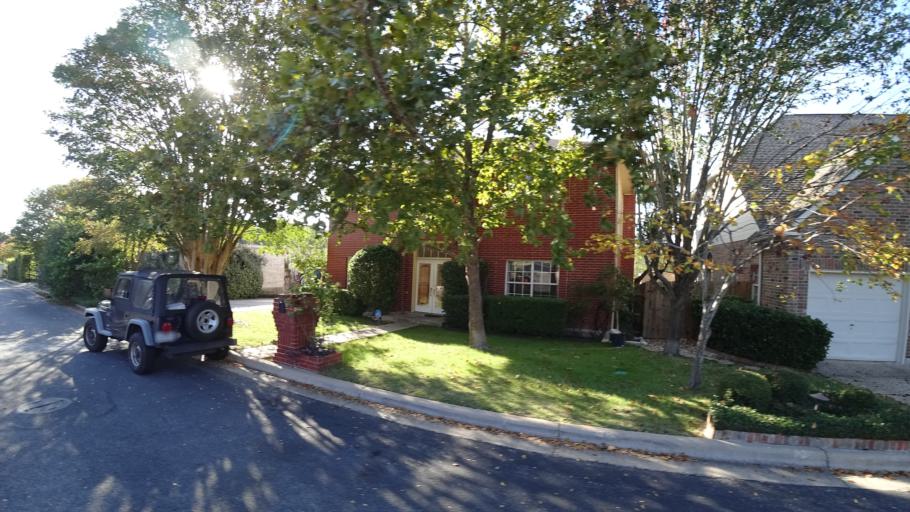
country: US
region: Texas
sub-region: Williamson County
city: Anderson Mill
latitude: 30.4311
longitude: -97.8138
